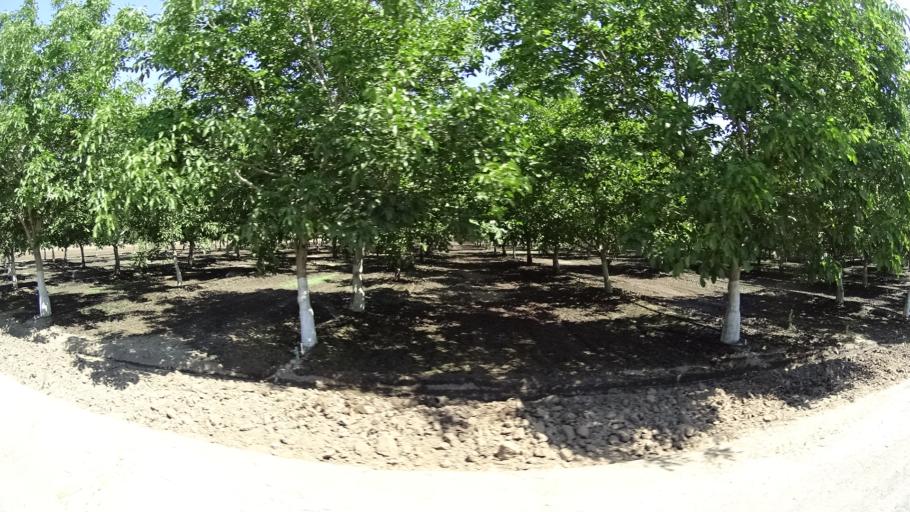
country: US
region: California
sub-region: Kings County
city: Lucerne
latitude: 36.3717
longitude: -119.6948
